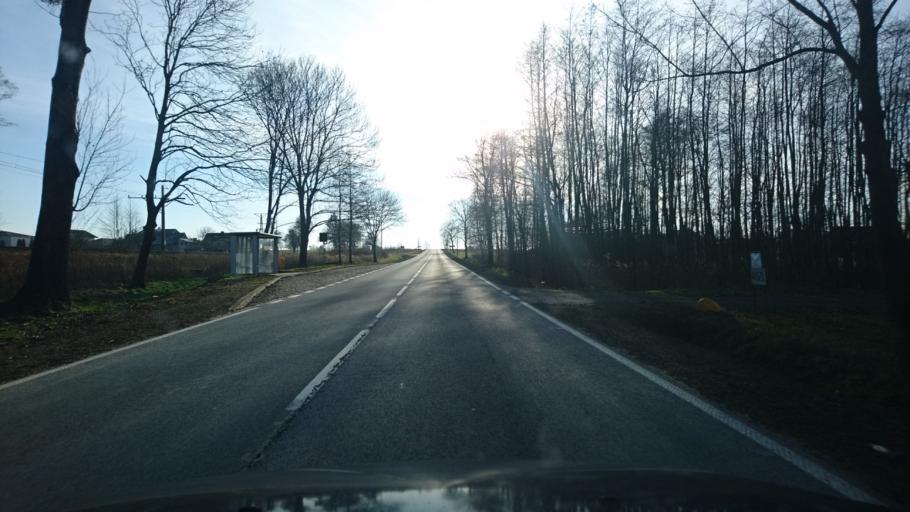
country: PL
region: Opole Voivodeship
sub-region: Powiat oleski
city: Dalachow
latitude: 51.0661
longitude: 18.6009
